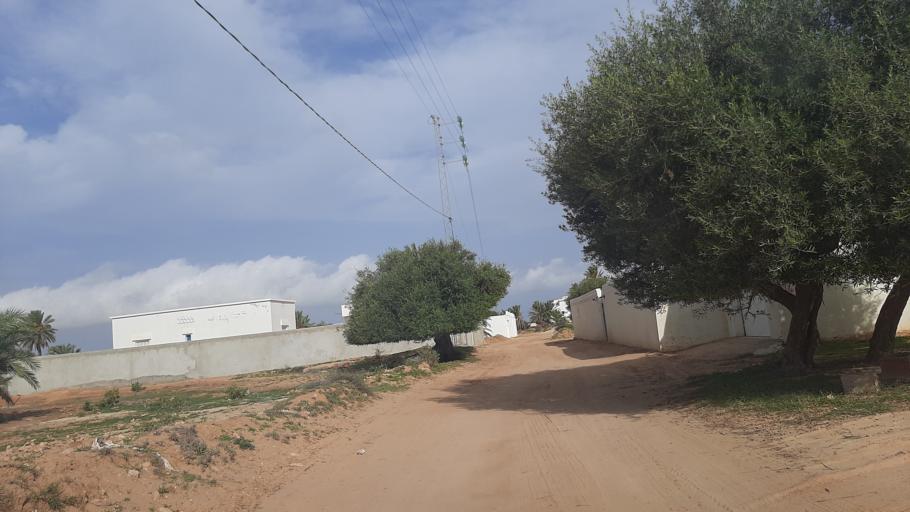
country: TN
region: Madanin
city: Midoun
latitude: 33.8018
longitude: 11.0264
